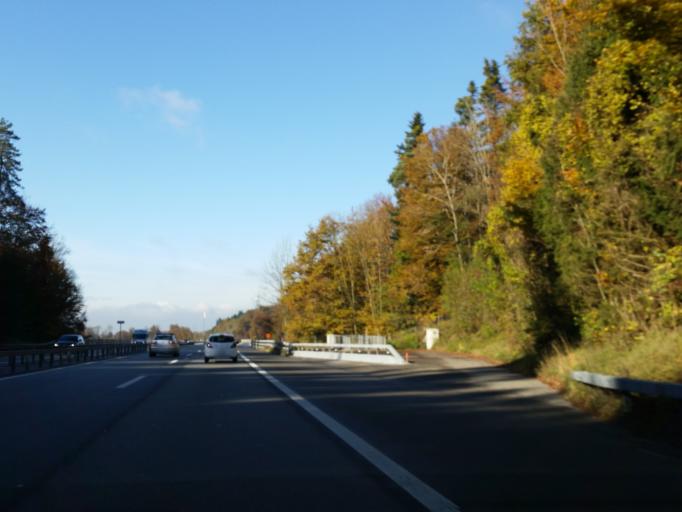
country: CH
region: Bern
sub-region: Bern-Mittelland District
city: Muhleberg
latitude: 46.9612
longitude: 7.2538
